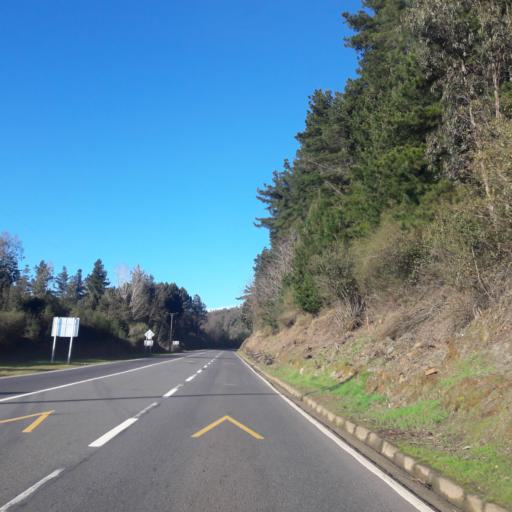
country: CL
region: Biobio
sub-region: Provincia de Biobio
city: La Laja
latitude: -37.2636
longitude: -72.9607
